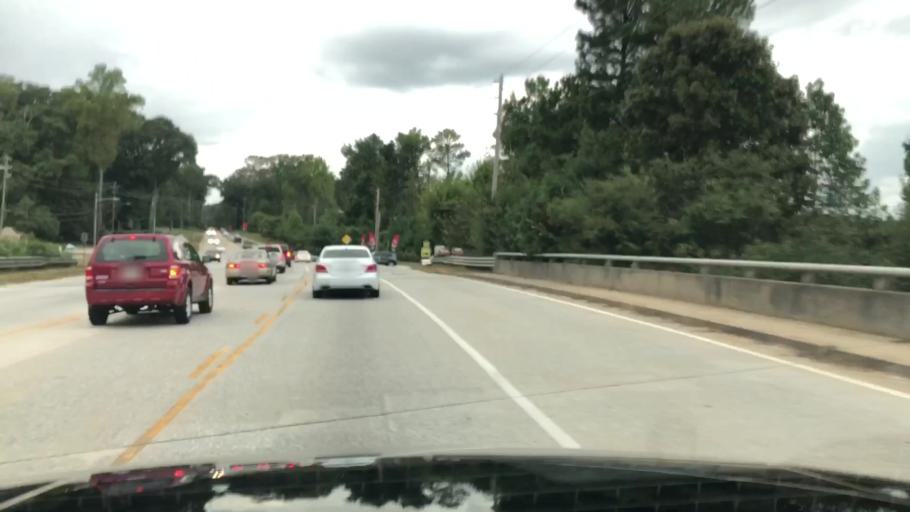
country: US
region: Georgia
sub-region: Fulton County
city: College Park
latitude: 33.6933
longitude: -84.5180
